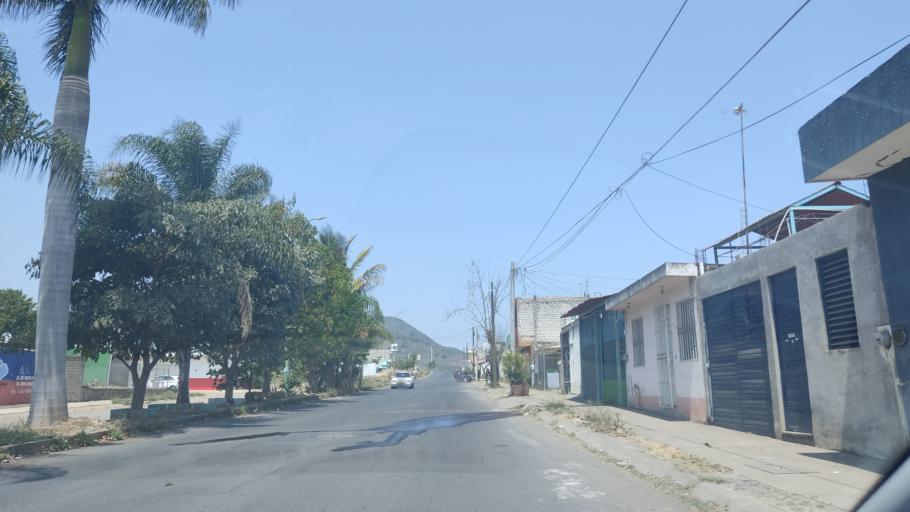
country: MX
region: Nayarit
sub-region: Tepic
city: La Corregidora
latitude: 21.4898
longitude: -104.8166
